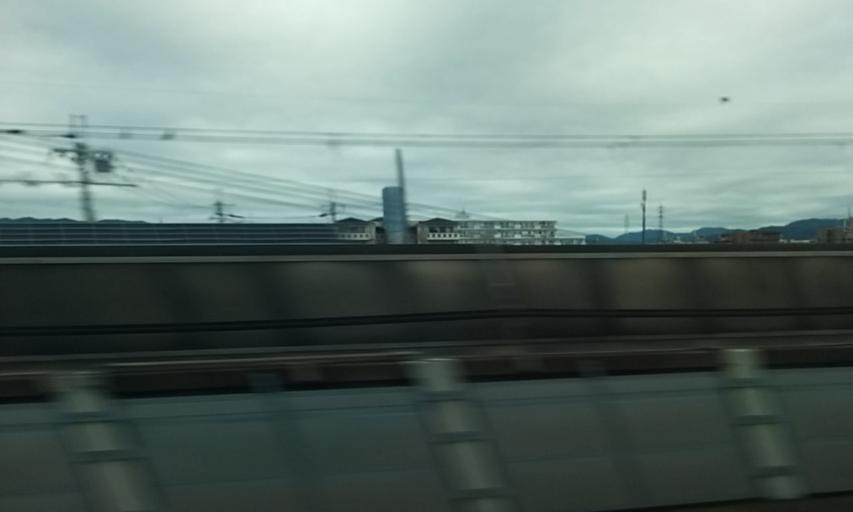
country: JP
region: Hyogo
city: Itami
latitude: 34.7676
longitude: 135.3906
